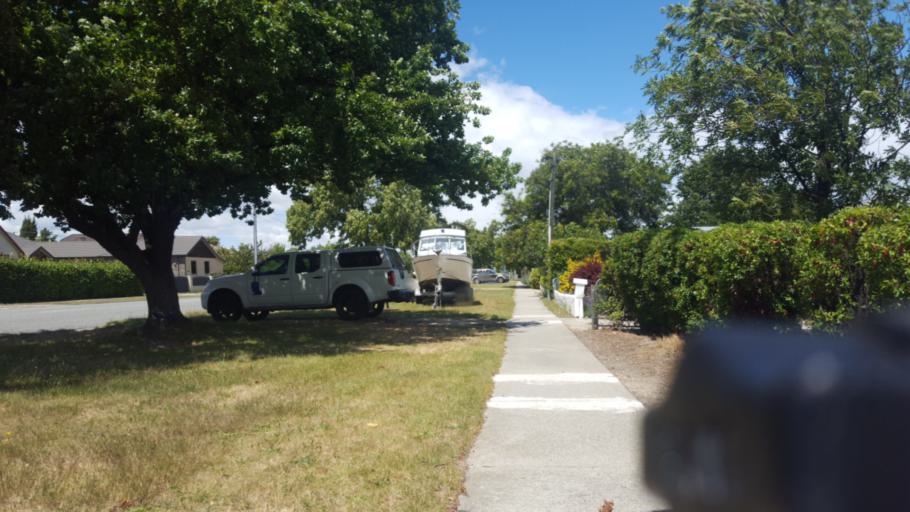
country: NZ
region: Otago
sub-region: Queenstown-Lakes District
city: Wanaka
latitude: -45.1899
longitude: 169.3201
